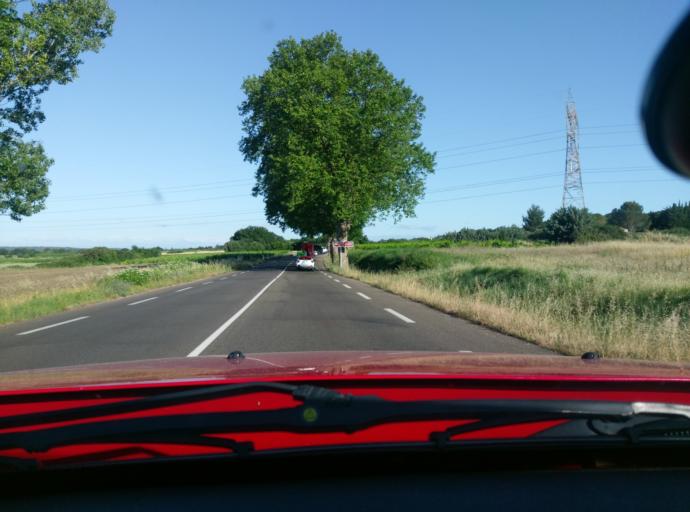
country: FR
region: Languedoc-Roussillon
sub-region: Departement du Gard
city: Uzes
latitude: 43.9818
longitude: 4.4677
